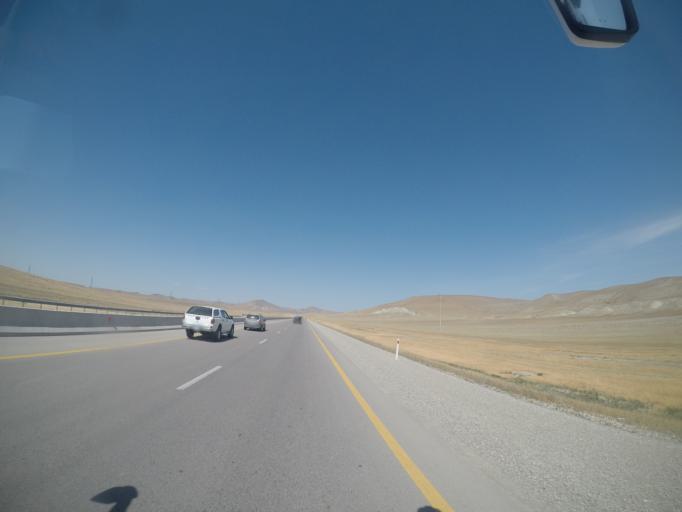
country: AZ
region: Sumqayit
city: Haci Zeynalabdin
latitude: 40.4949
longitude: 49.3551
